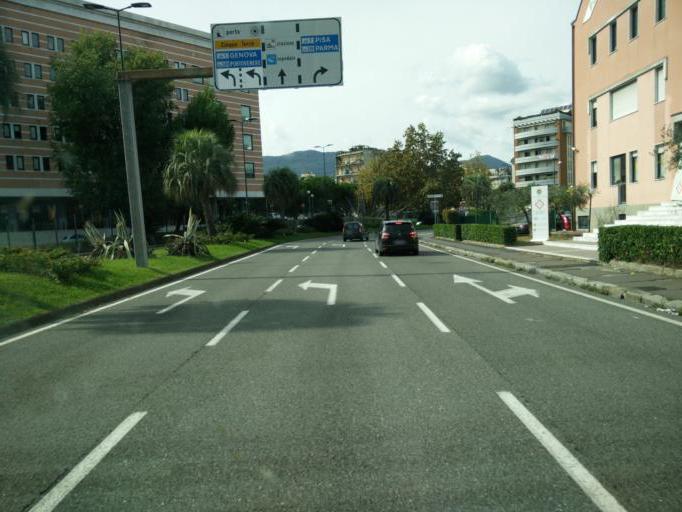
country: IT
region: Liguria
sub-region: Provincia di La Spezia
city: La Spezia
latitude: 44.1136
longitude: 9.8399
